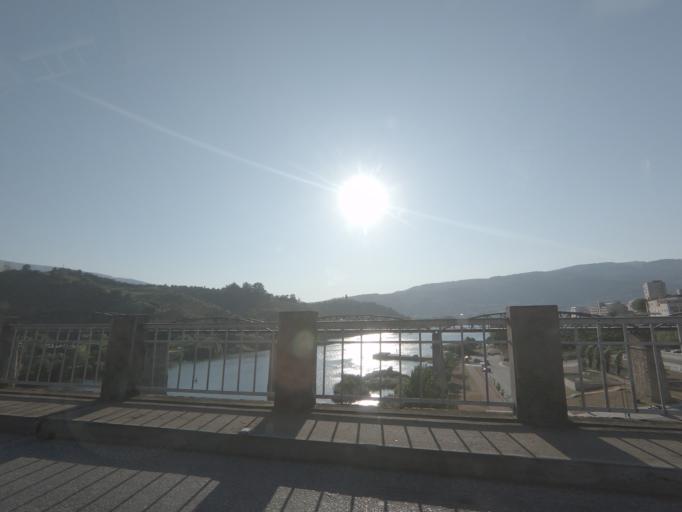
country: PT
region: Vila Real
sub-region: Peso da Regua
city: Peso da Regua
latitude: 41.1549
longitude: -7.7800
